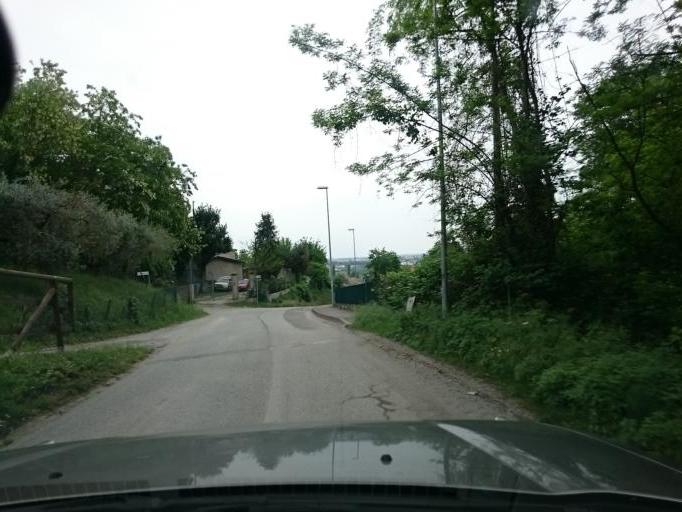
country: IT
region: Veneto
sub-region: Provincia di Padova
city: Montegrotto Terme
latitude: 45.3161
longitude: 11.7798
